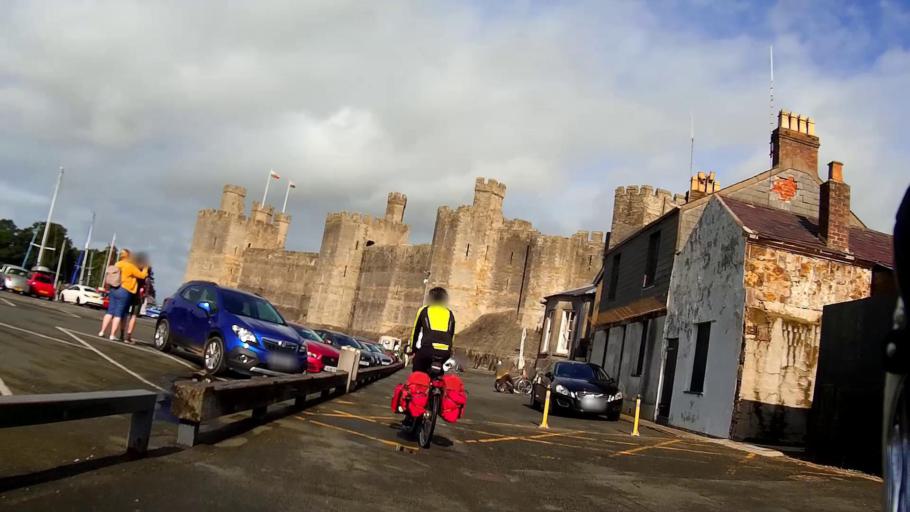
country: GB
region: Wales
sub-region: Gwynedd
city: Caernarfon
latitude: 53.1386
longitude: -4.2750
